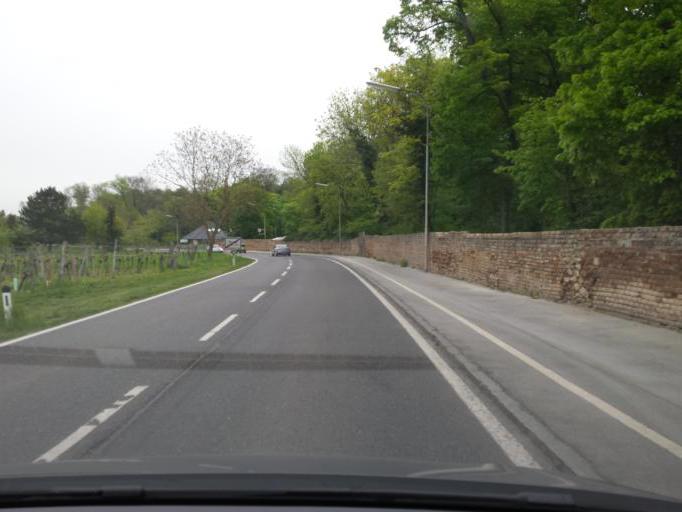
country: AT
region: Burgenland
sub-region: Politischer Bezirk Neusiedl am See
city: Bruckneudorf
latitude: 48.0274
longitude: 16.7841
